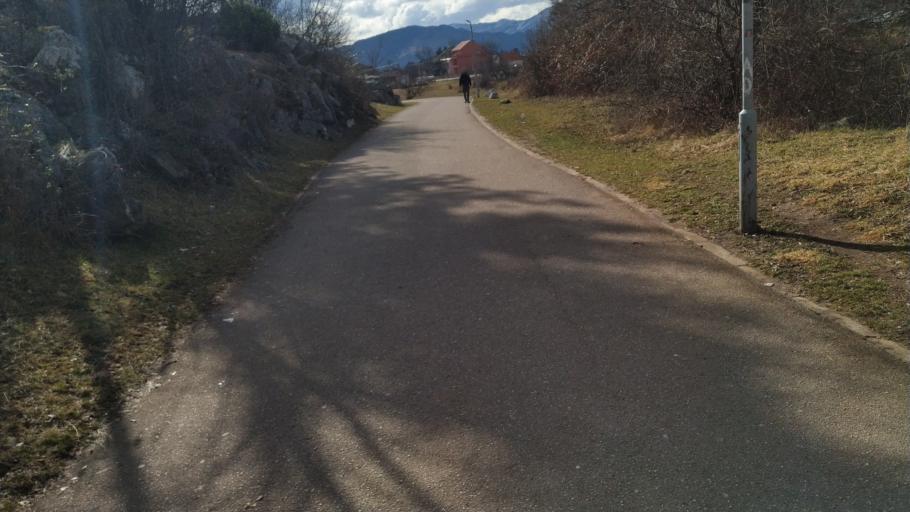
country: ME
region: Opstina Niksic
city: Niksic
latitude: 42.7661
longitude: 18.9559
